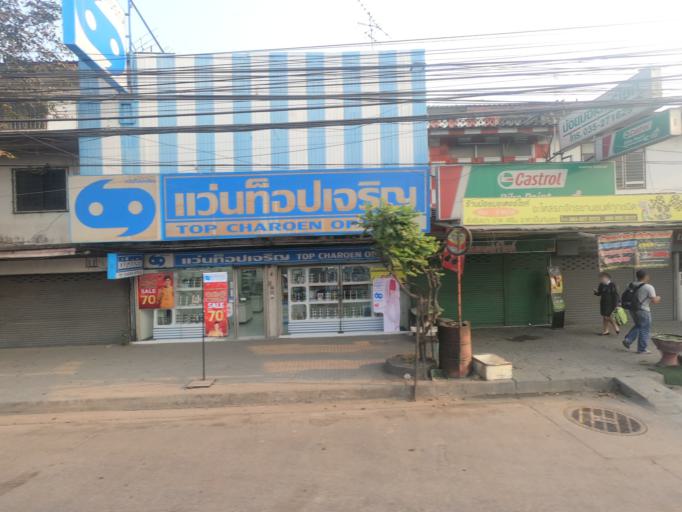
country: TH
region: Phra Nakhon Si Ayutthaya
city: Wang Noi
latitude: 14.2315
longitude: 100.7157
